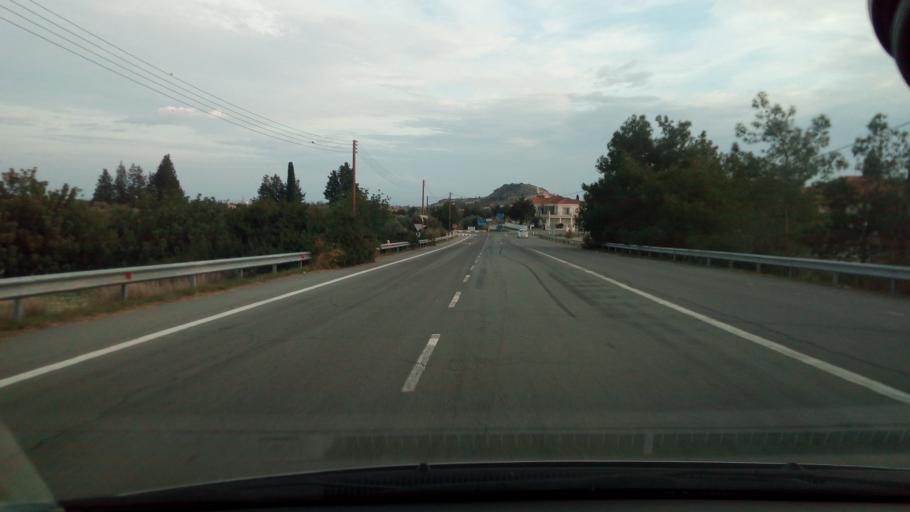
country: CY
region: Larnaka
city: Kofinou
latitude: 34.8522
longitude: 33.4502
